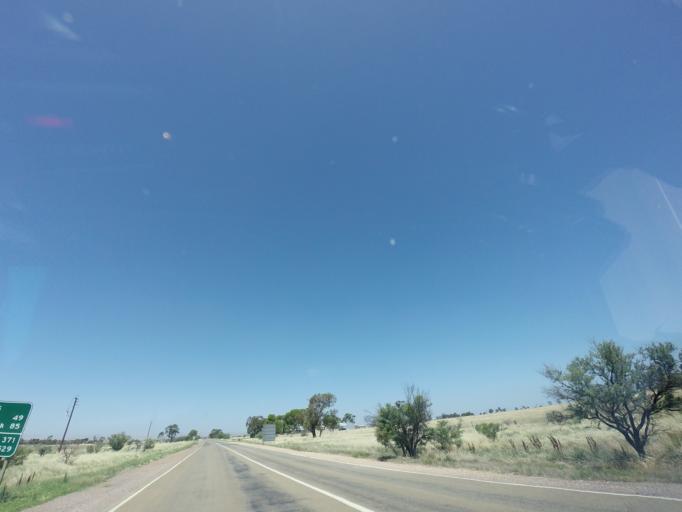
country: AU
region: South Australia
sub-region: Flinders Ranges
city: Quorn
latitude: -32.6660
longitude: 138.1130
